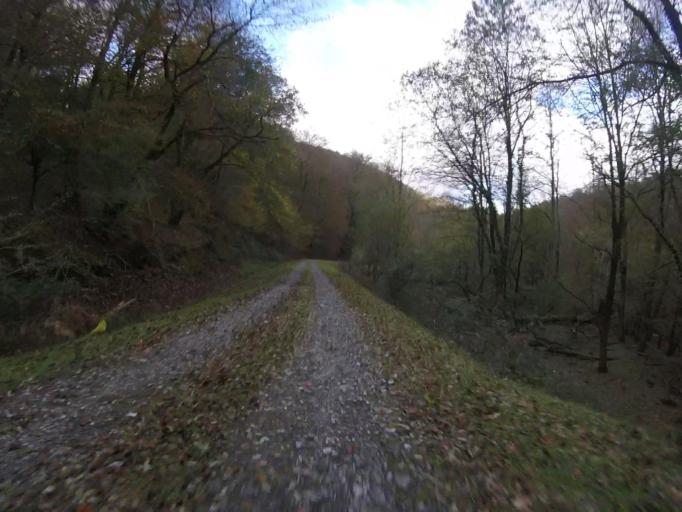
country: ES
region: Navarre
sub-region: Provincia de Navarra
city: Goizueta
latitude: 43.1822
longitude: -1.7989
